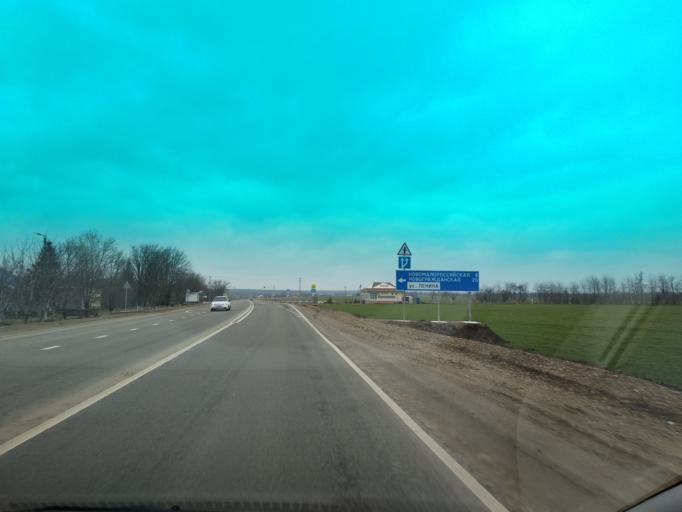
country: RU
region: Krasnodarskiy
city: Novomalorossiyskaya
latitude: 45.7083
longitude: 39.8490
